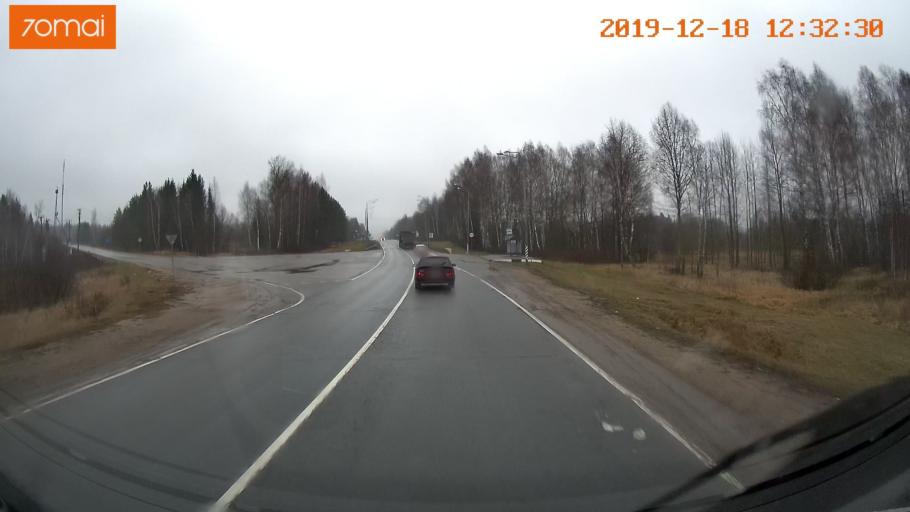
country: RU
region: Moskovskaya
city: Rumyantsevo
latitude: 56.1060
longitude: 36.5514
